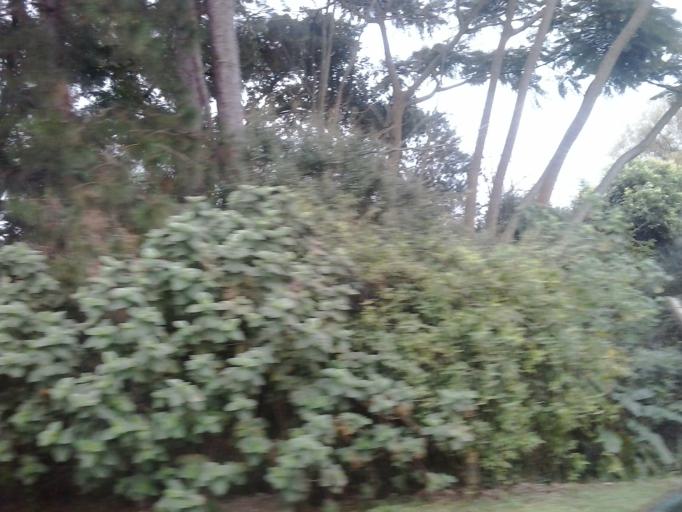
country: BR
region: Rio Grande do Sul
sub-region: Santa Maria
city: Santa Maria
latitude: -29.7220
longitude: -53.7180
